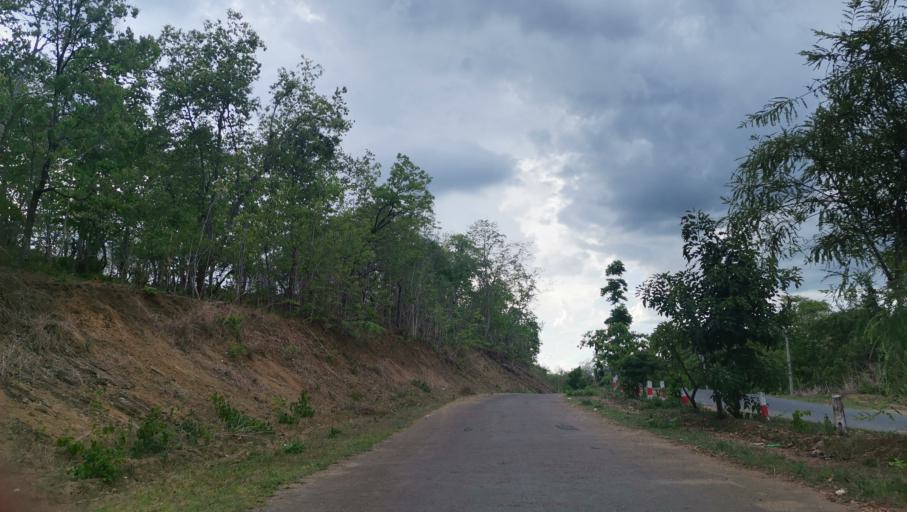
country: MM
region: Magway
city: Minbu
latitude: 20.1038
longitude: 94.5482
